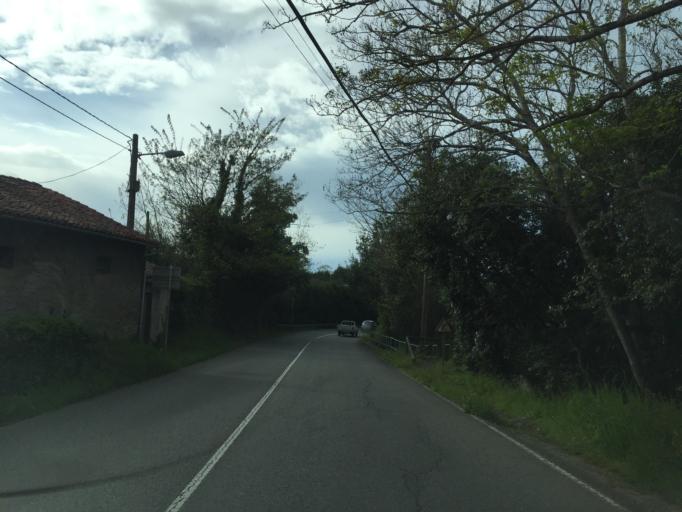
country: ES
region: Asturias
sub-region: Province of Asturias
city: Gijon
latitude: 43.5198
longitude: -5.6089
